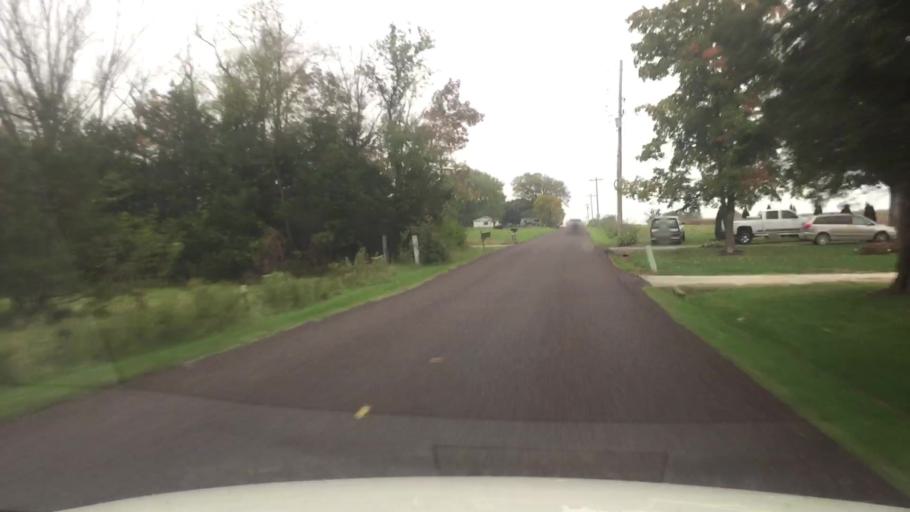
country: US
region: Missouri
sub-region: Boone County
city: Ashland
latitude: 38.8110
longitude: -92.2749
